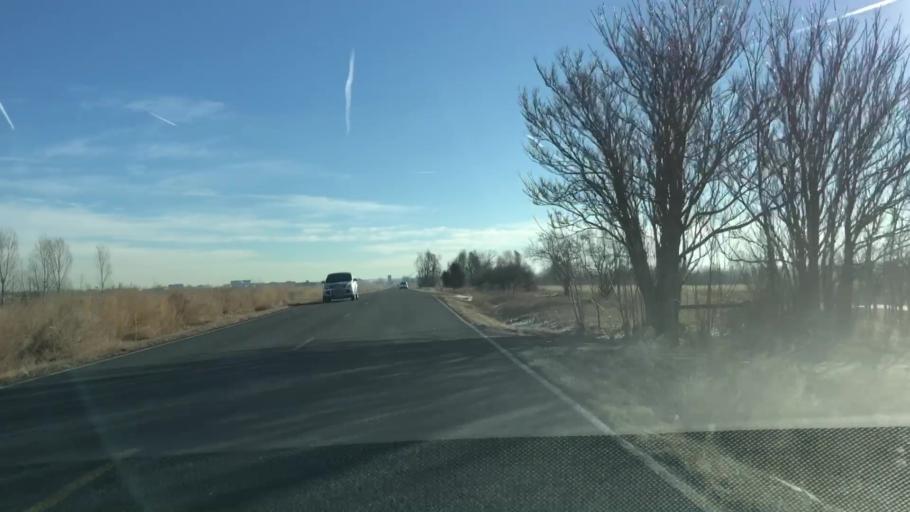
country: US
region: Colorado
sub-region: Larimer County
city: Loveland
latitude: 40.3999
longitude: -105.0155
